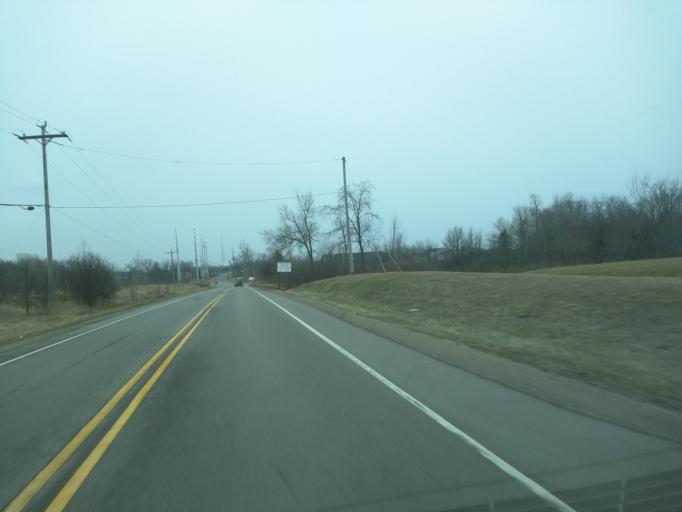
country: US
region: Michigan
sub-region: Eaton County
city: Waverly
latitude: 42.7158
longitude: -84.6229
